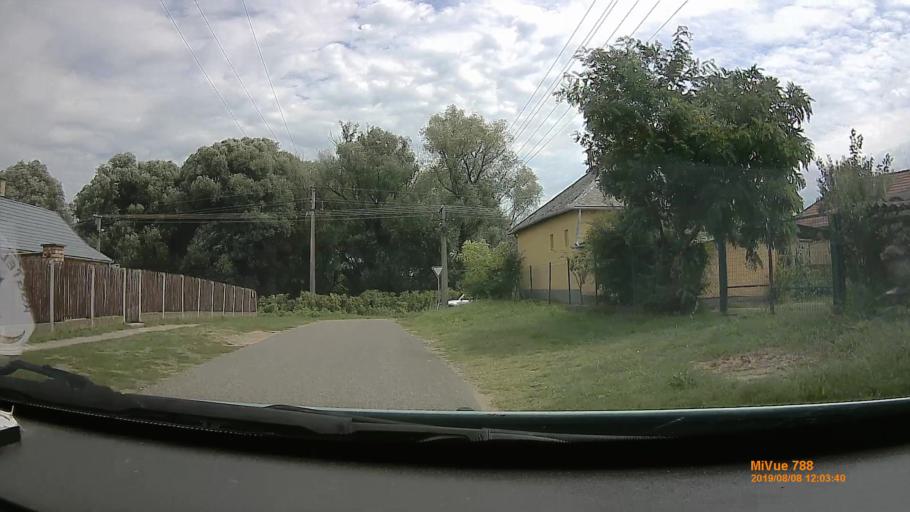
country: HU
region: Szabolcs-Szatmar-Bereg
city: Nyirbogat
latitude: 47.7938
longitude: 22.0559
